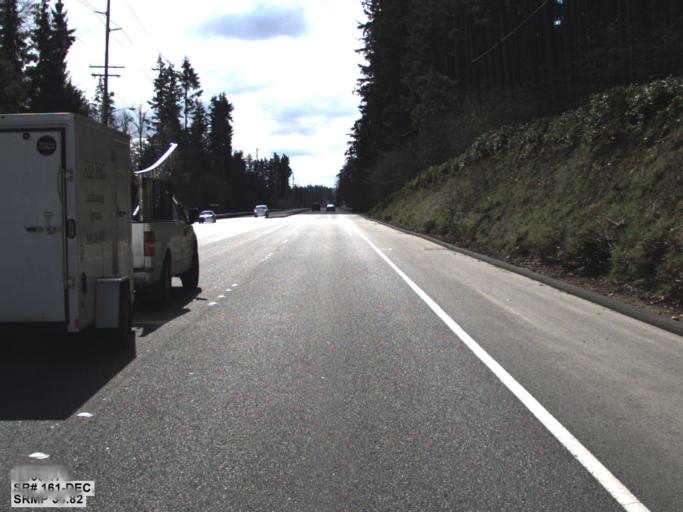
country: US
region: Washington
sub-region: King County
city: Lakeland South
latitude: 47.2701
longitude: -122.3040
